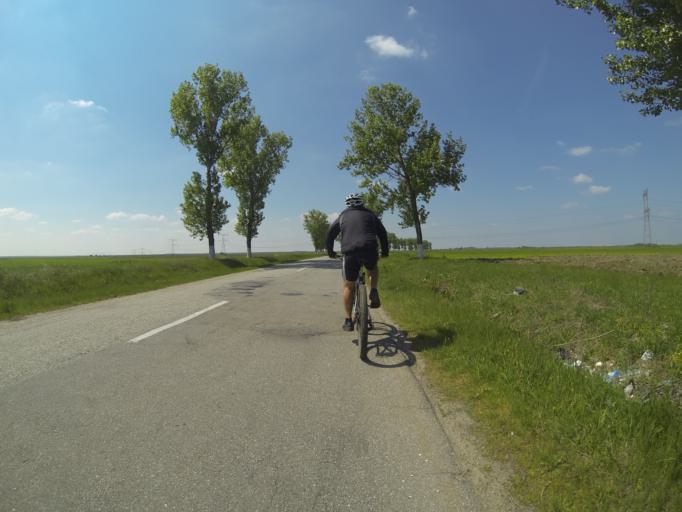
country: RO
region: Dolj
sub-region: Comuna Terpezita
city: Terpezita
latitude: 44.2942
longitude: 23.5575
